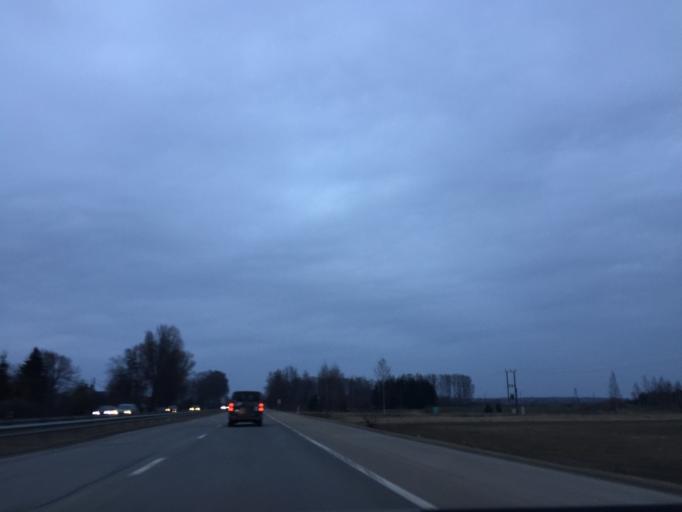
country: LV
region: Olaine
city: Olaine
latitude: 56.7801
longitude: 23.9425
